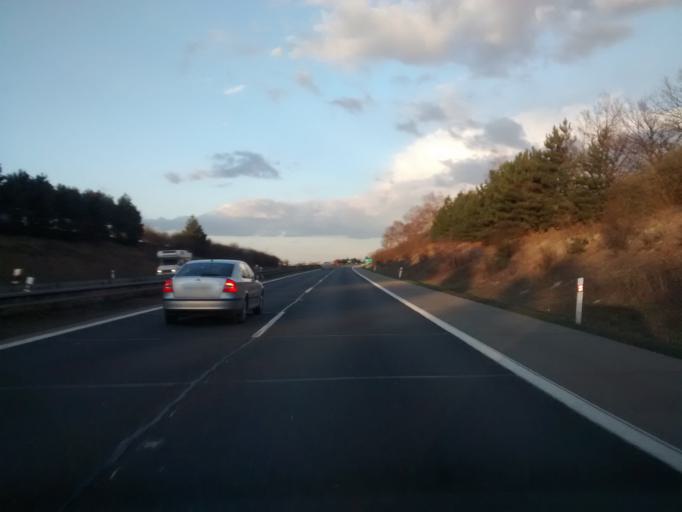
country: CZ
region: Central Bohemia
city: Prerov nad Labem
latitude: 50.1359
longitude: 14.8245
